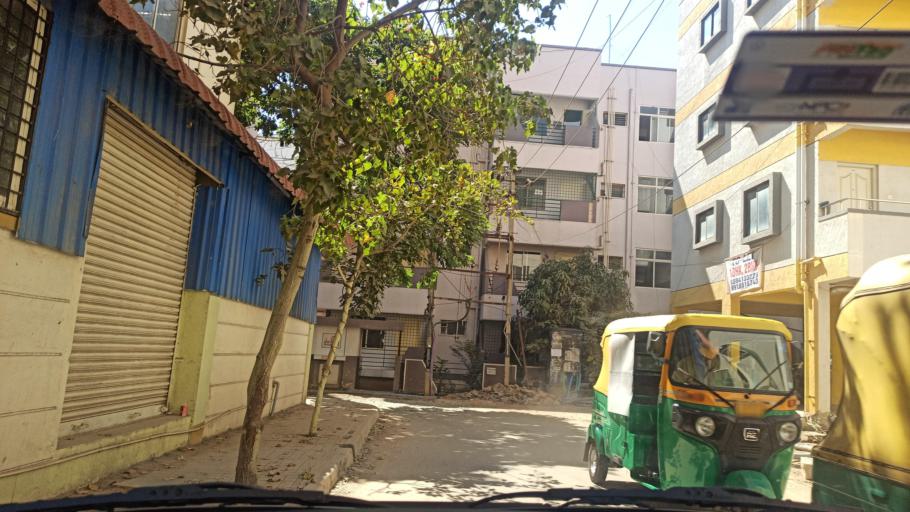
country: IN
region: Karnataka
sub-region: Bangalore Urban
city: Bangalore
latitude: 12.9249
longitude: 77.6718
